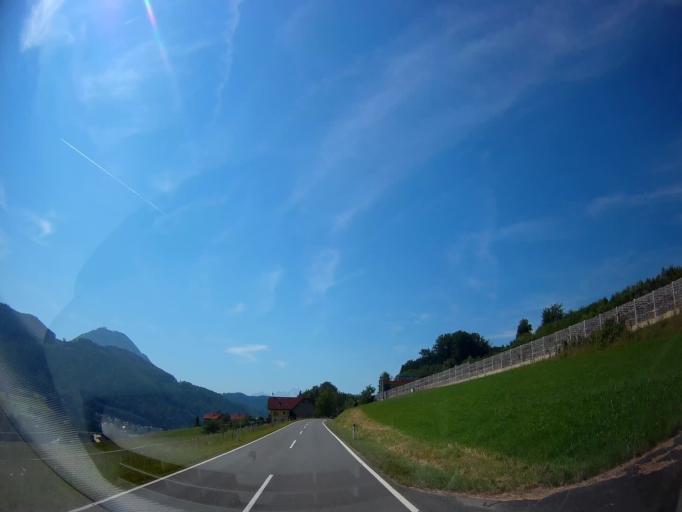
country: AT
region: Salzburg
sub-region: Politischer Bezirk Salzburg-Umgebung
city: Hallwang
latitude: 47.8459
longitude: 13.0798
